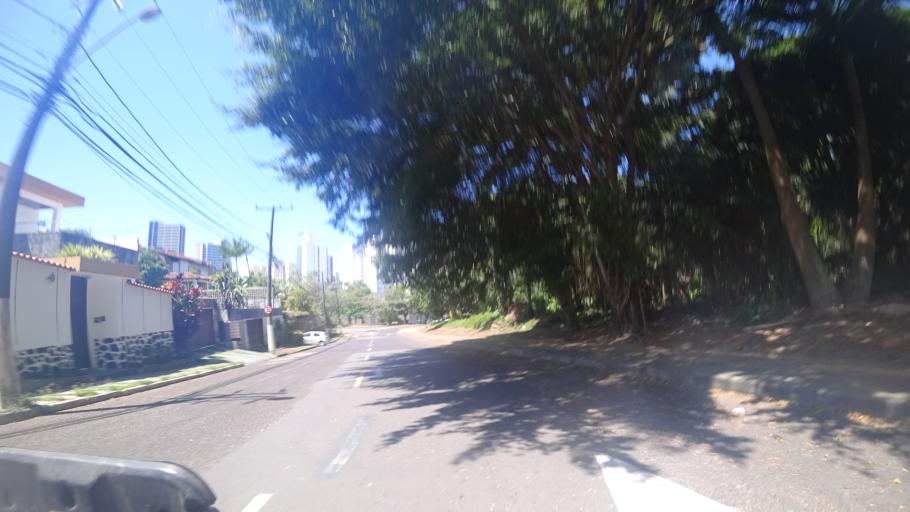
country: BR
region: Bahia
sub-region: Salvador
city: Salvador
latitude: -12.9915
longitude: -38.4687
